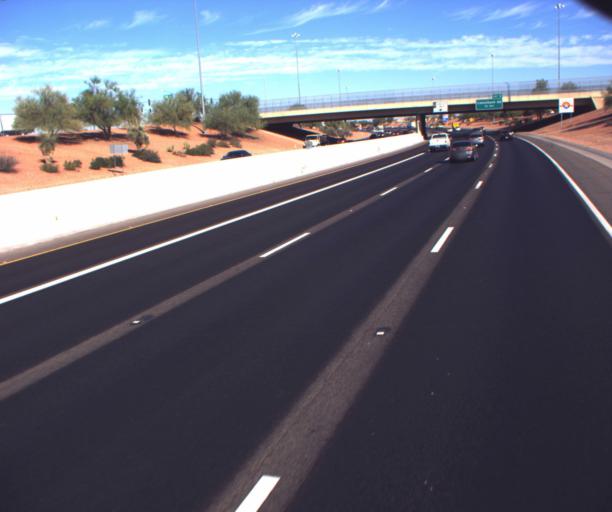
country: US
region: Arizona
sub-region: Maricopa County
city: Tolleson
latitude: 33.4926
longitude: -112.2637
